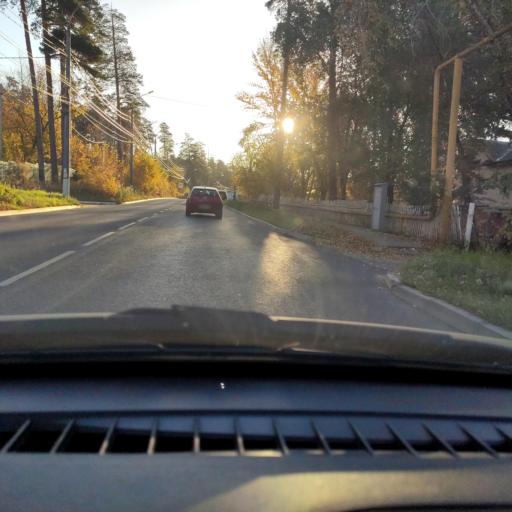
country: RU
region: Samara
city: Tol'yatti
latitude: 53.4753
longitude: 49.3745
